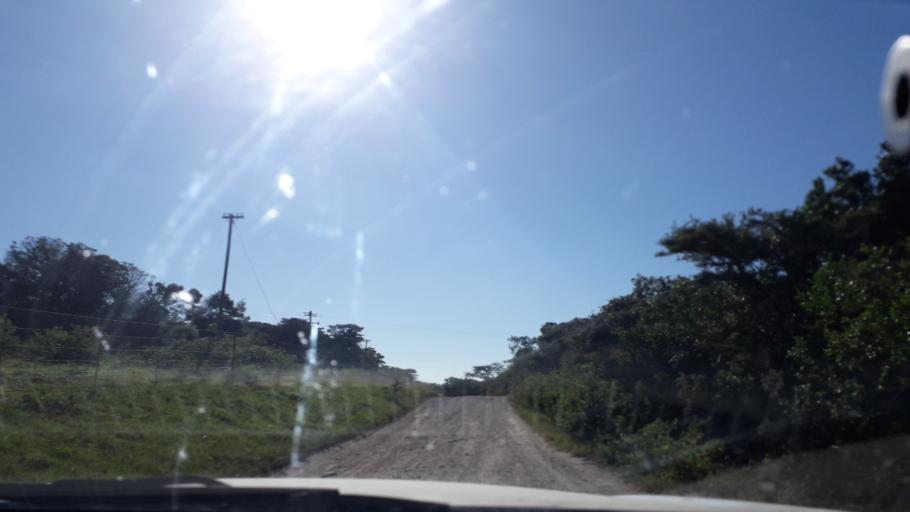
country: ZA
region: Eastern Cape
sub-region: Buffalo City Metropolitan Municipality
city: East London
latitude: -32.8430
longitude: 27.9726
